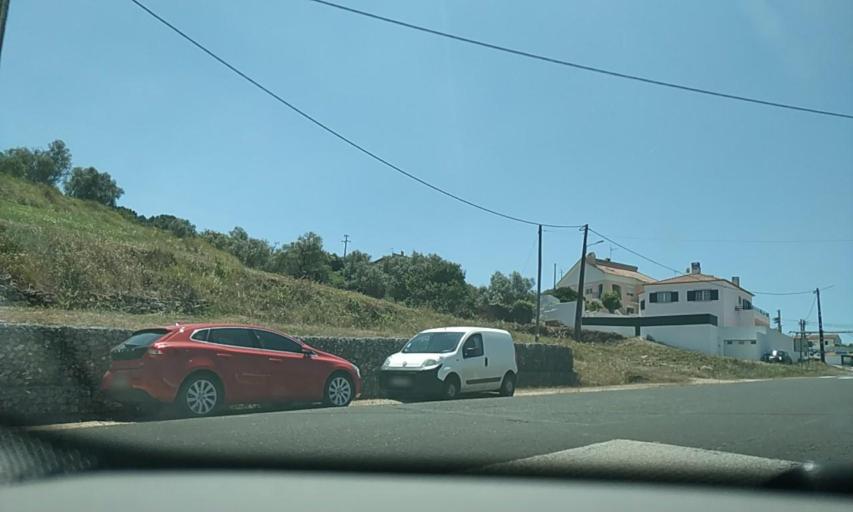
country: PT
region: Lisbon
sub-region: Sintra
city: Almargem
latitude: 38.8766
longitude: -9.2495
